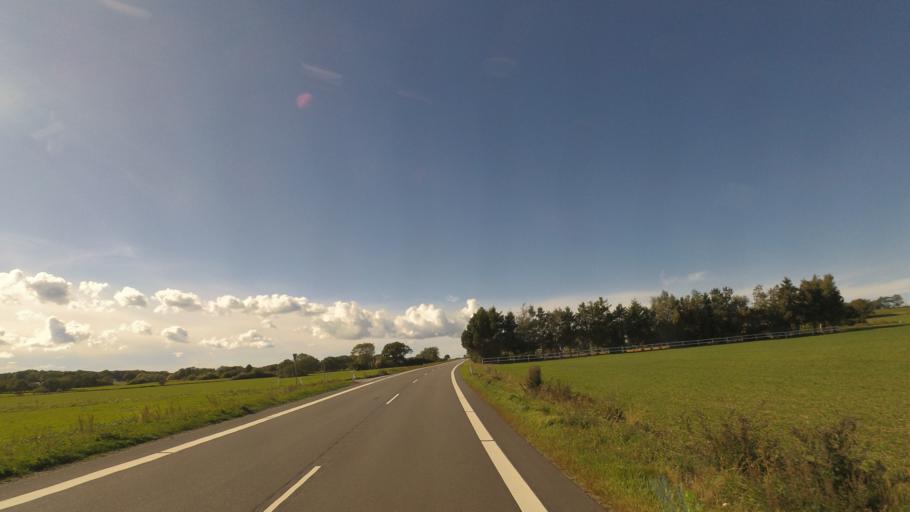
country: DK
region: Capital Region
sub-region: Bornholm Kommune
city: Akirkeby
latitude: 55.0690
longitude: 14.9749
